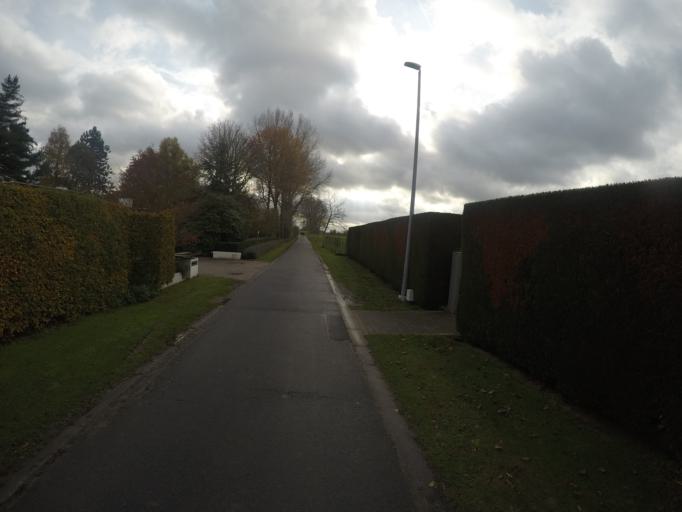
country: BE
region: Flanders
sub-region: Provincie Oost-Vlaanderen
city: Hamme
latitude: 51.1304
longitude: 4.1407
